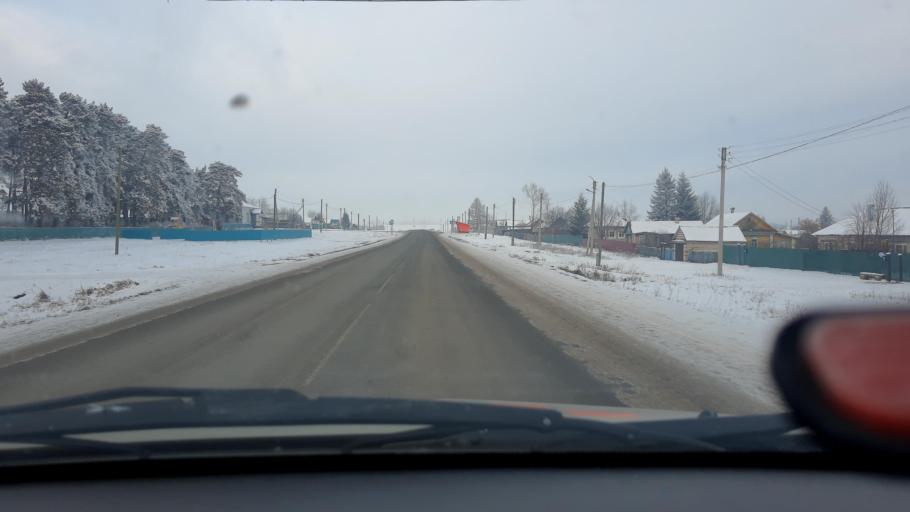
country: RU
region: Bashkortostan
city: Avdon
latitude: 54.3784
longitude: 55.8094
